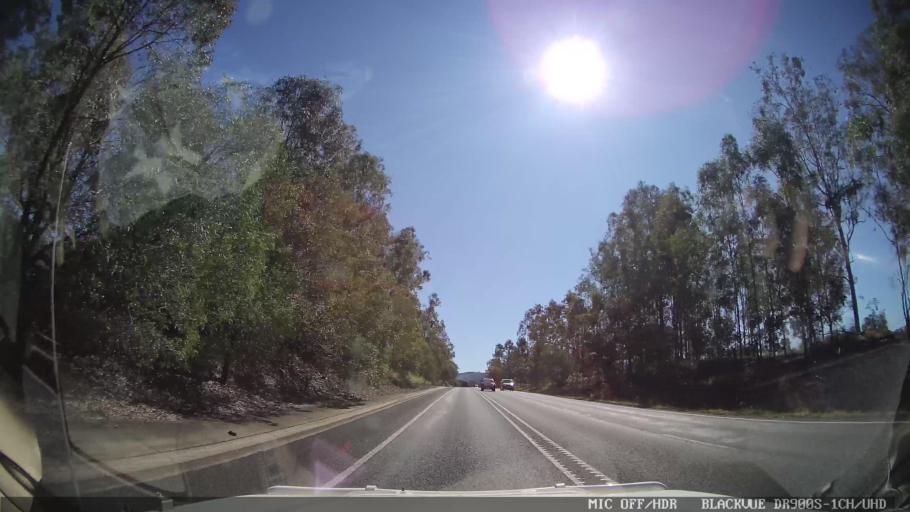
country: AU
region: Queensland
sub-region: Gympie Regional Council
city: Gympie
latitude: -26.0012
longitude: 152.5665
